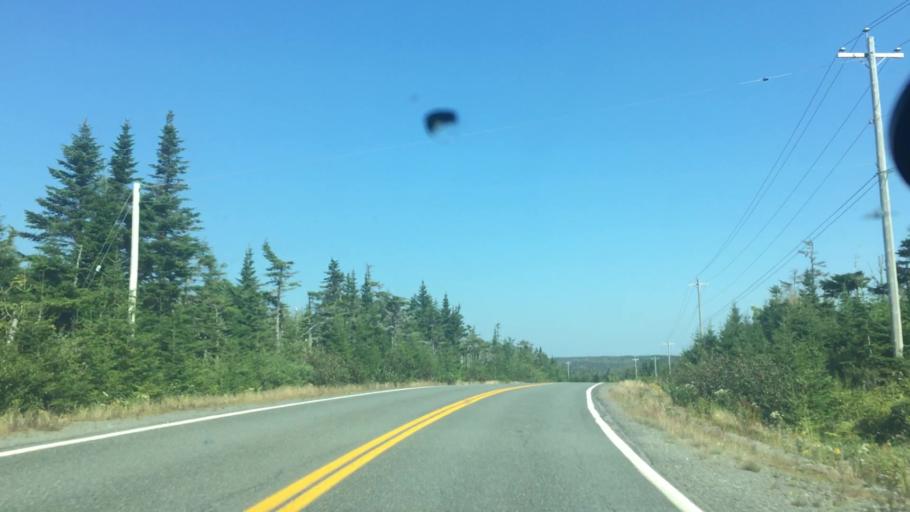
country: CA
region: Nova Scotia
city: Antigonish
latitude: 44.9871
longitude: -62.0969
